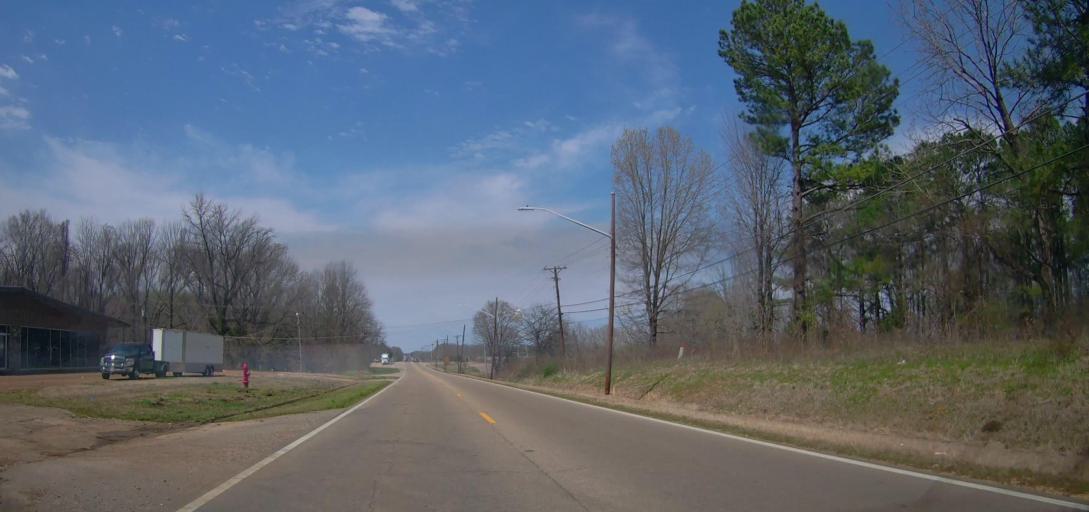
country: US
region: Mississippi
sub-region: Union County
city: New Albany
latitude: 34.5138
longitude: -89.0415
